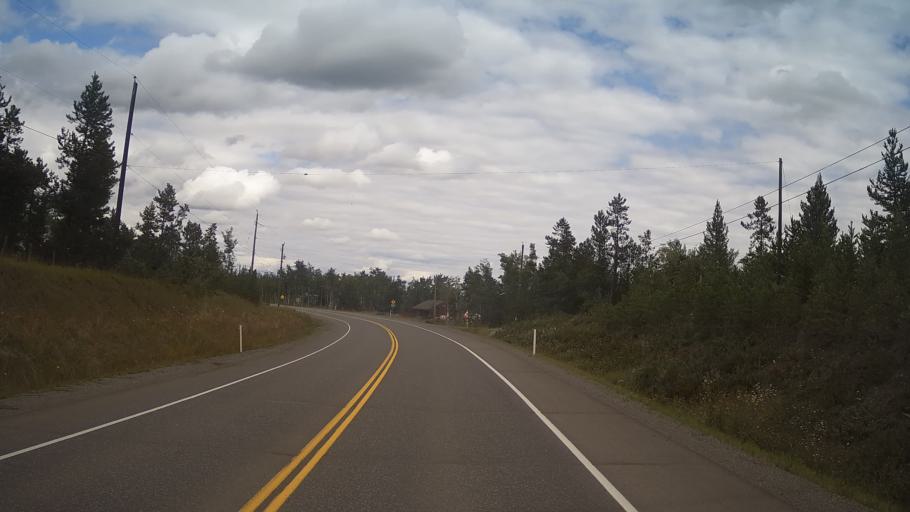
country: CA
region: British Columbia
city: Cache Creek
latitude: 51.3134
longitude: -121.3918
